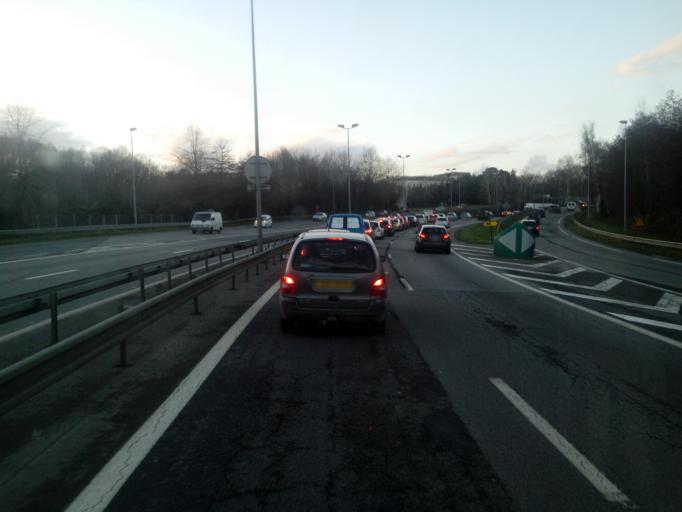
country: FR
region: Pays de la Loire
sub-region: Departement de la Loire-Atlantique
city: La Chapelle-sur-Erdre
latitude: 47.2580
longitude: -1.5541
